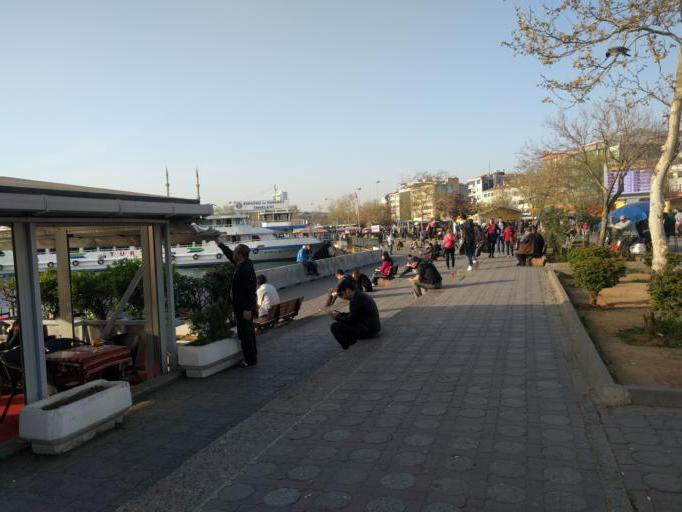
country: TR
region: Istanbul
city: UEskuedar
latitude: 40.9930
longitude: 29.0240
